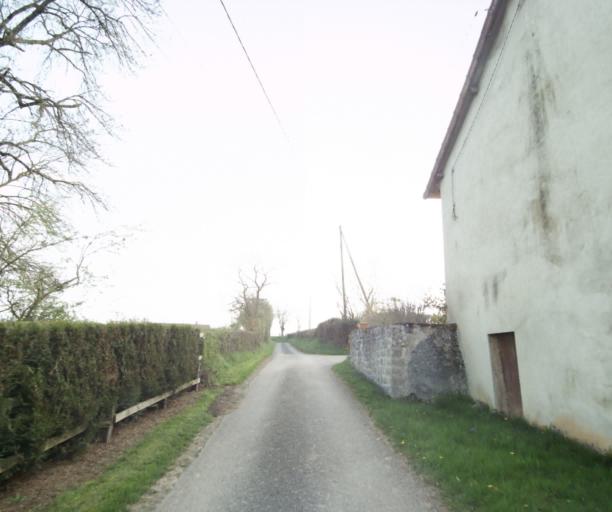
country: FR
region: Bourgogne
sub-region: Departement de Saone-et-Loire
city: Charolles
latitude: 46.4647
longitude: 4.4306
